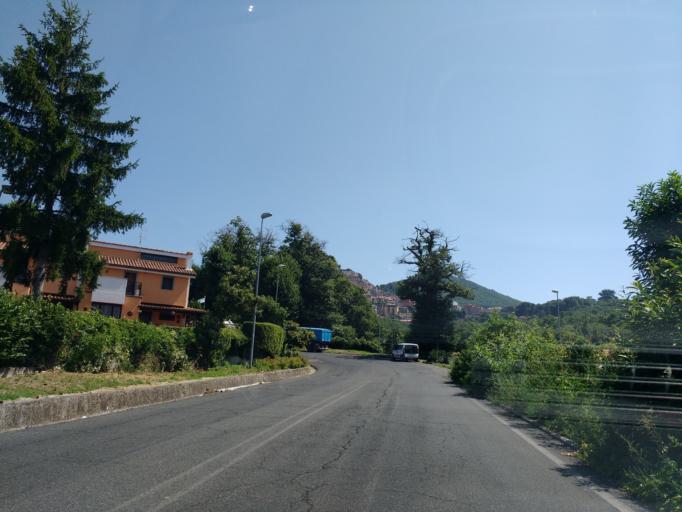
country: IT
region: Latium
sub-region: Citta metropolitana di Roma Capitale
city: Rocca di Papa
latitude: 41.7704
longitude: 12.7058
